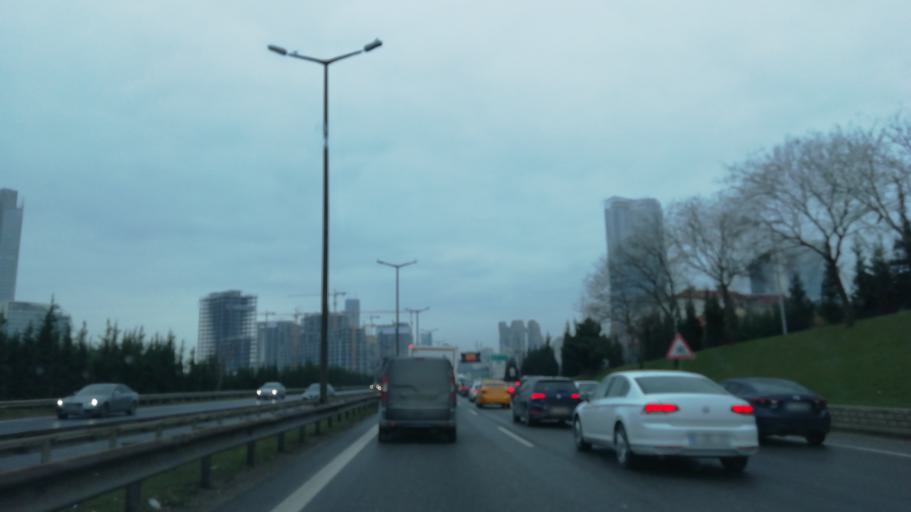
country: TR
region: Istanbul
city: Umraniye
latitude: 41.0064
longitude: 29.0986
